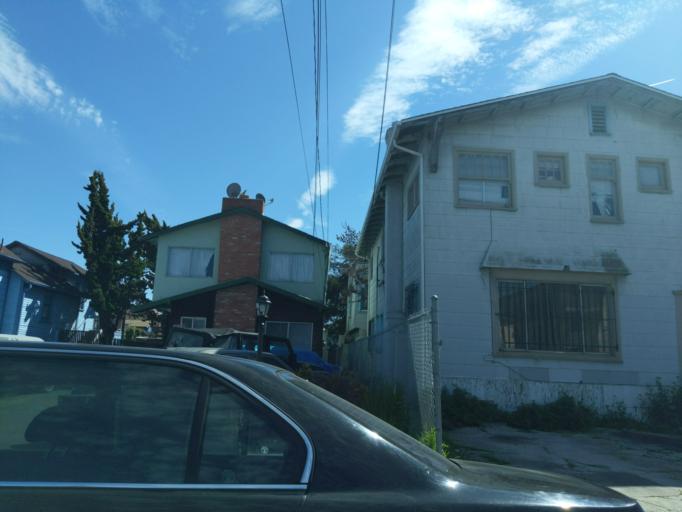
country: US
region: California
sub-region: Alameda County
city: Alameda
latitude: 37.7761
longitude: -122.2190
